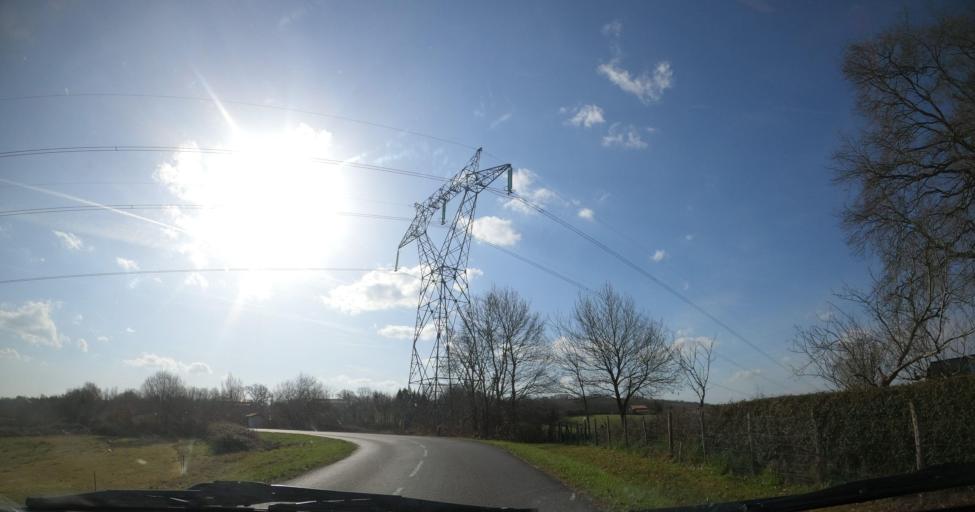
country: FR
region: Aquitaine
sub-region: Departement des Pyrenees-Atlantiques
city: Briscous
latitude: 43.4480
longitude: -1.3711
